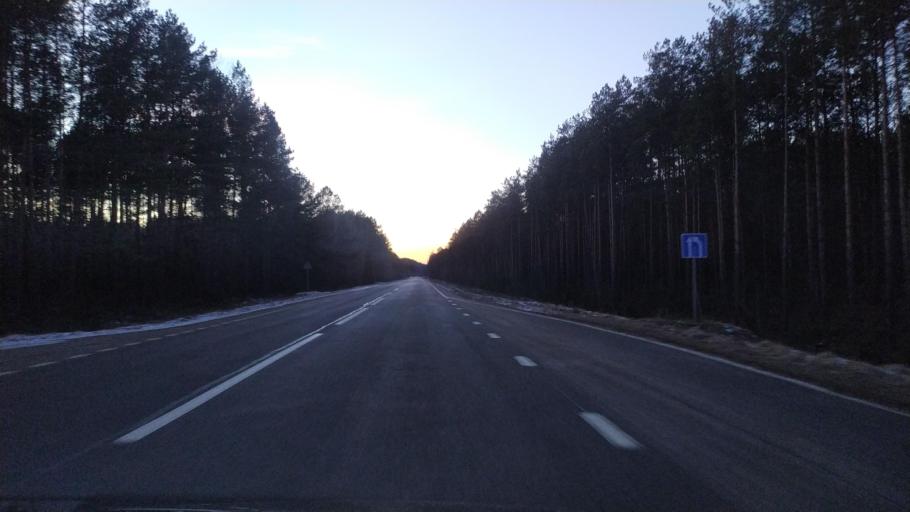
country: BY
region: Brest
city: Zhabinka
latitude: 52.3983
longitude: 24.0343
